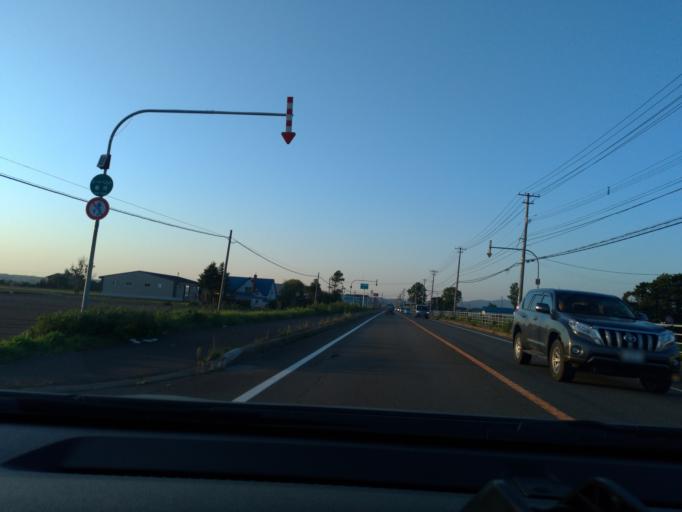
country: JP
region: Hokkaido
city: Tobetsu
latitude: 43.1973
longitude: 141.5228
